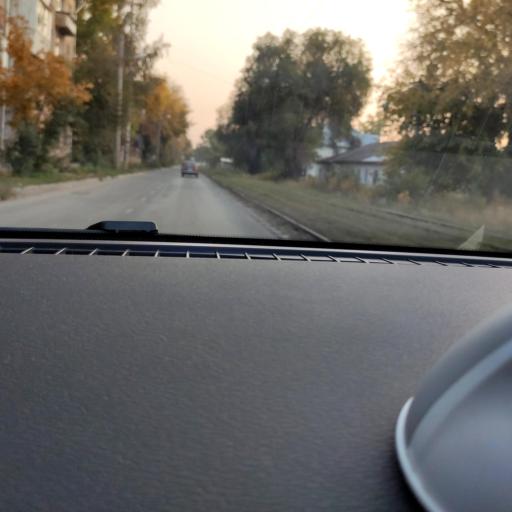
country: RU
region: Samara
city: Petra-Dubrava
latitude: 53.2315
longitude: 50.2854
